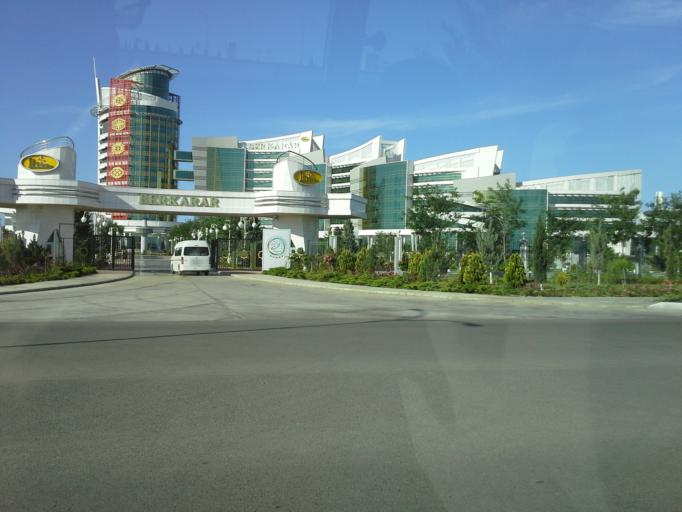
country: TM
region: Balkan
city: Turkmenbasy
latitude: 39.9629
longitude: 52.8353
